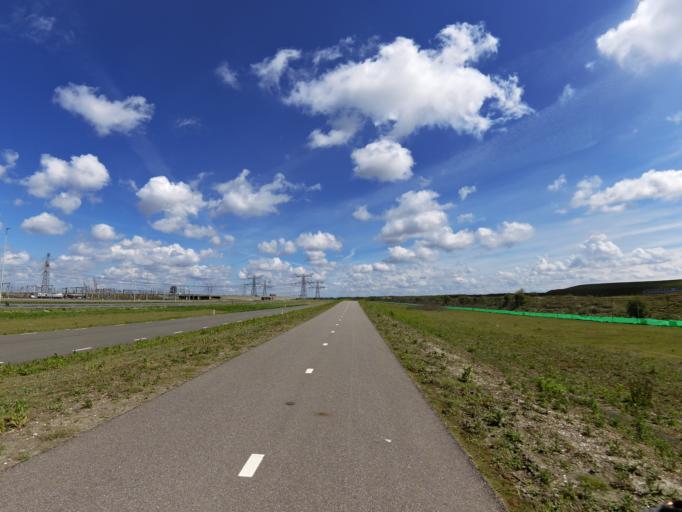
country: NL
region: South Holland
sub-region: Gemeente Rotterdam
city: Hoek van Holland
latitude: 51.9296
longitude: 4.0274
